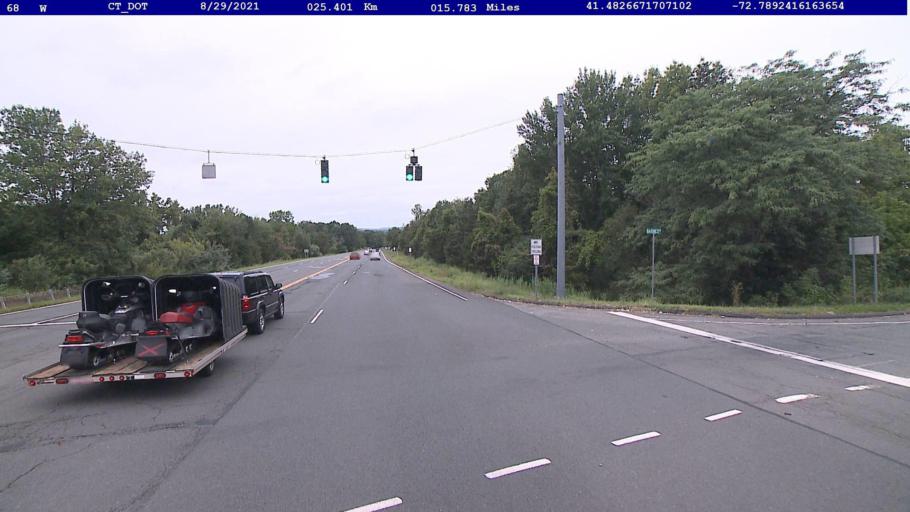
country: US
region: Connecticut
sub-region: New Haven County
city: Wallingford
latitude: 41.4831
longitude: -72.7898
